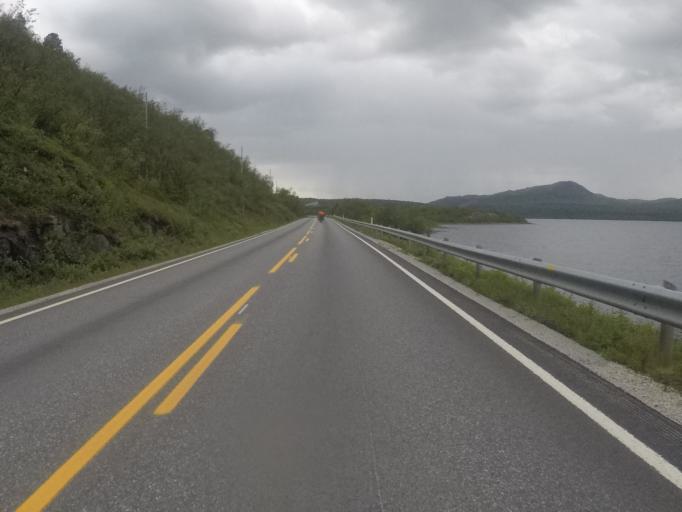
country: NO
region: Finnmark Fylke
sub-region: Porsanger
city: Lakselv
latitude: 69.9164
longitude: 24.9812
